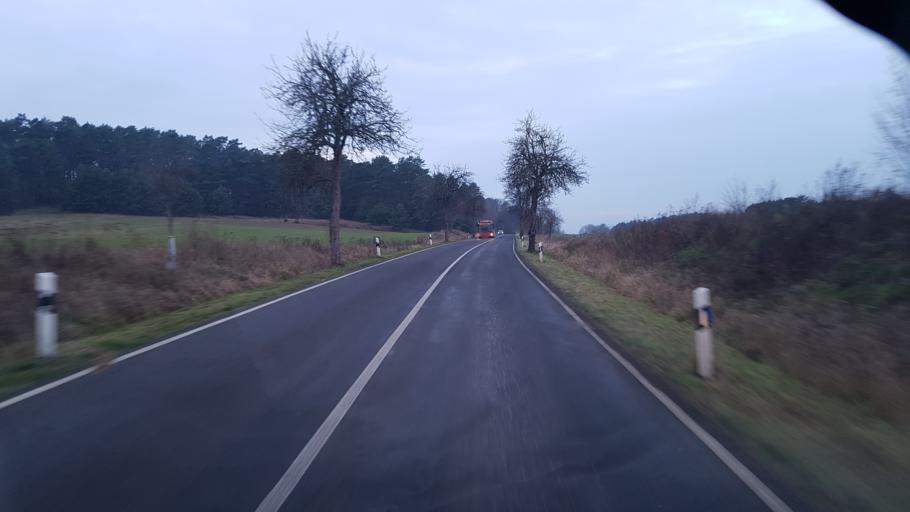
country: DE
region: Brandenburg
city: Wiesenau
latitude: 52.1817
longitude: 14.5642
